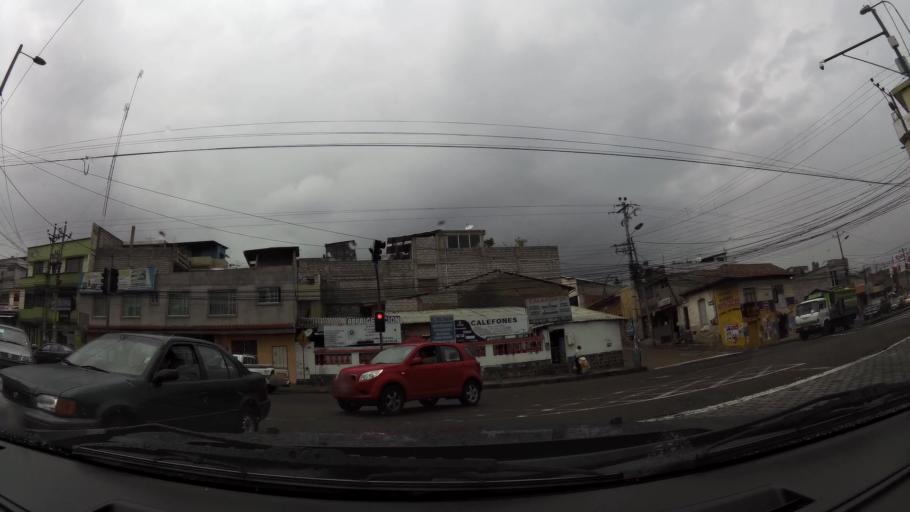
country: EC
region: Pichincha
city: Sangolqui
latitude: -0.3262
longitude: -78.4467
